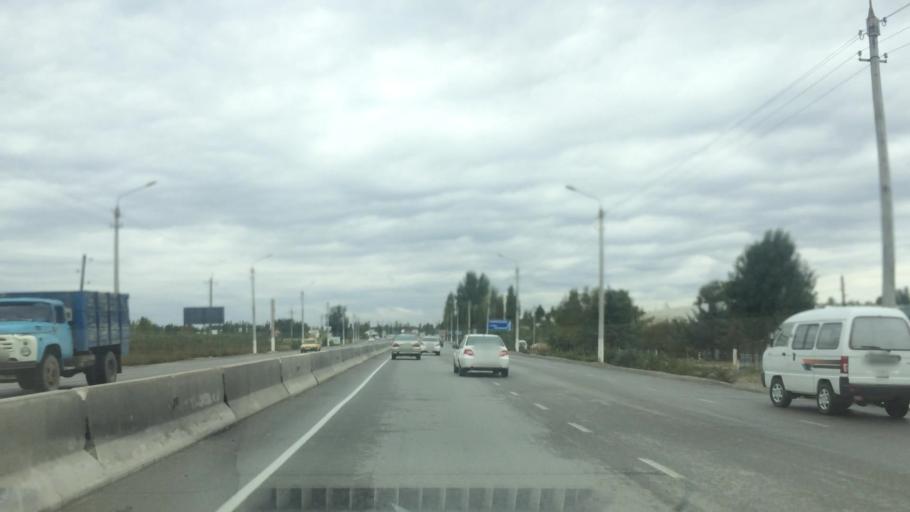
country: UZ
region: Jizzax
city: Jizzax
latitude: 39.9825
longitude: 67.5715
